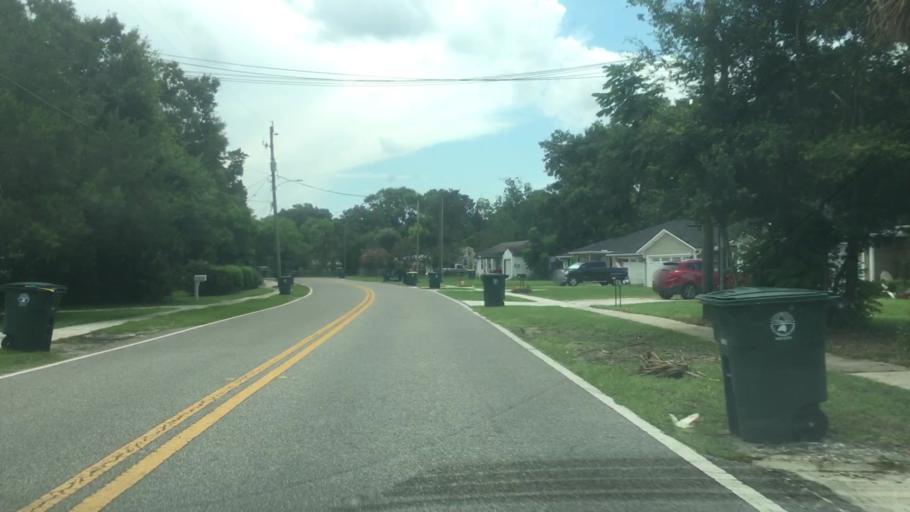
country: US
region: Florida
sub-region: Duval County
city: Jacksonville
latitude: 30.3052
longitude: -81.5492
